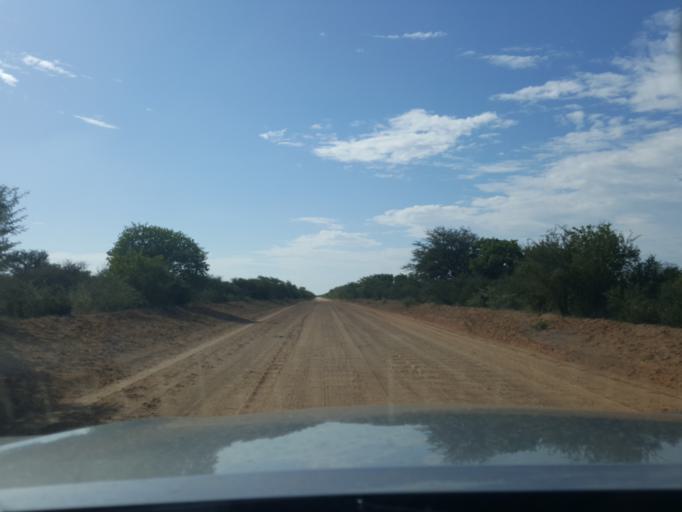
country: BW
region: Kweneng
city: Khudumelapye
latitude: -23.5037
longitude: 24.7080
